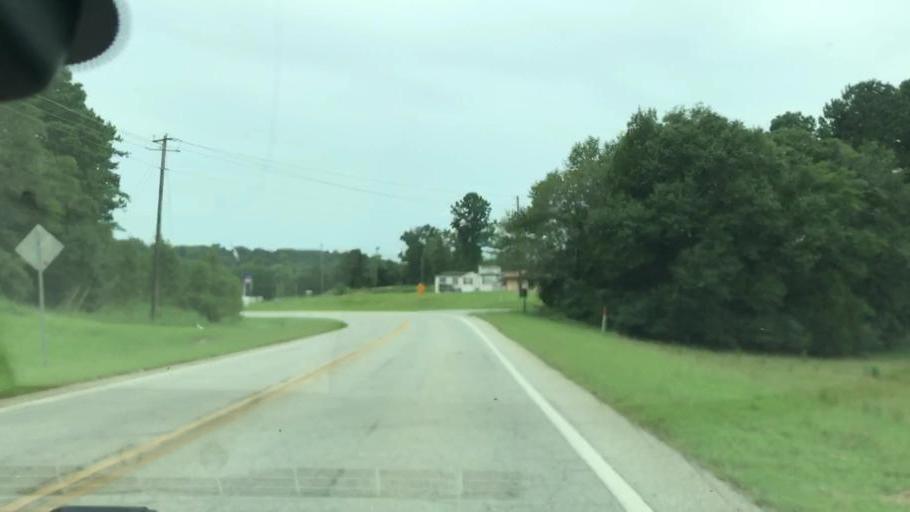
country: US
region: Georgia
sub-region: Clay County
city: Fort Gaines
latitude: 31.6295
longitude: -85.0458
